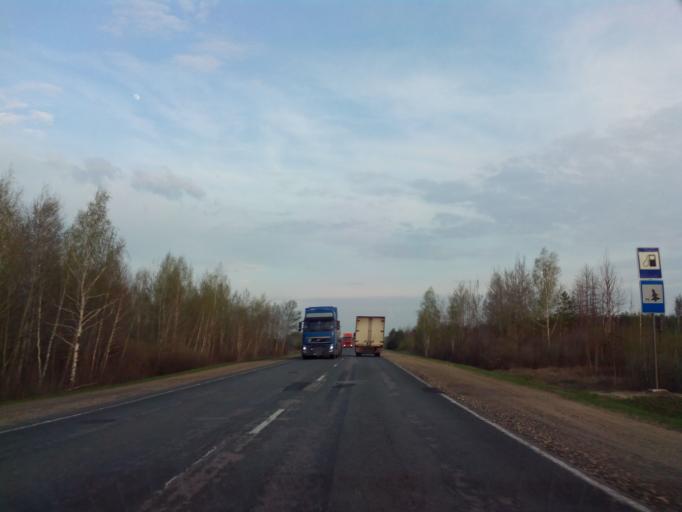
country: RU
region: Rjazan
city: Ryazhsk
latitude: 53.7250
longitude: 39.9078
